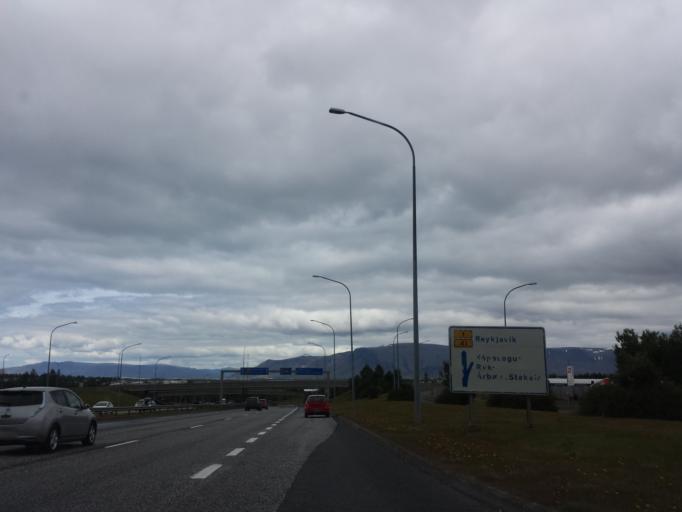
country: IS
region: Capital Region
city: Reykjavik
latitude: 64.1117
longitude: -21.8437
